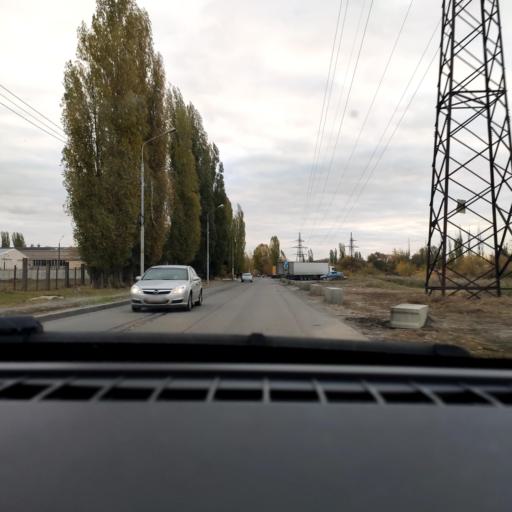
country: RU
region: Voronezj
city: Maslovka
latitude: 51.6233
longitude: 39.2489
